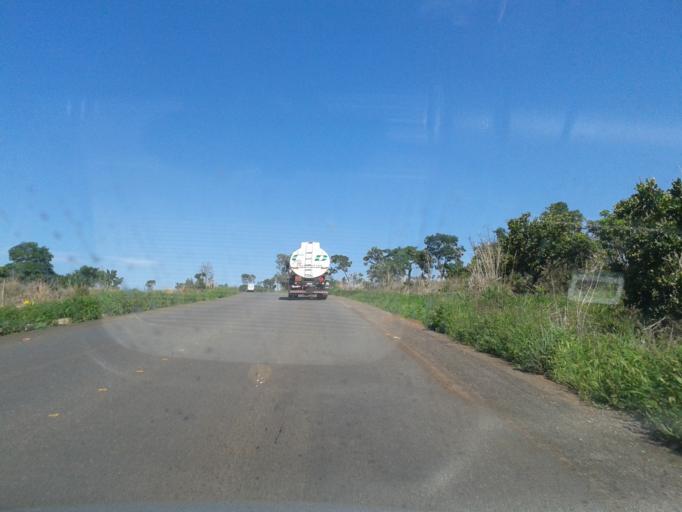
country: BR
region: Goias
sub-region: Bela Vista De Goias
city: Bela Vista de Goias
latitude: -17.0567
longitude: -48.9234
